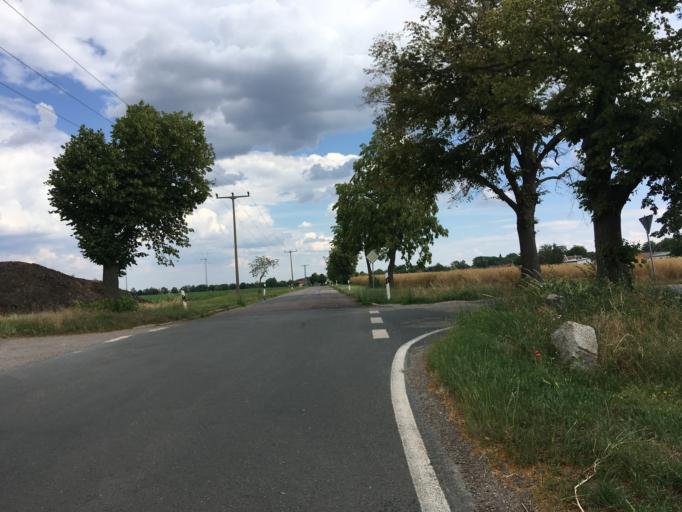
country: DE
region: Saxony-Anhalt
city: Baalberge
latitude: 51.7775
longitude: 11.8140
